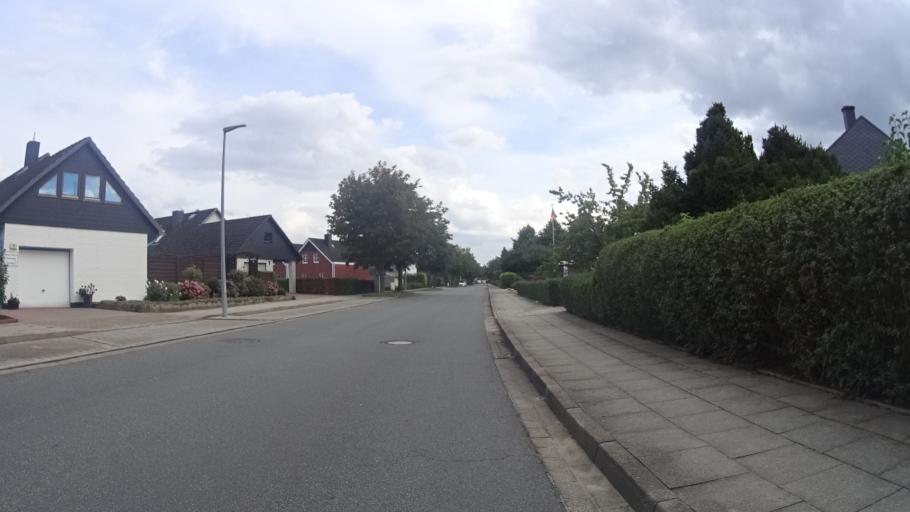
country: DE
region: Schleswig-Holstein
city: Blomesche Wildnis
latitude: 53.7969
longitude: 9.4148
